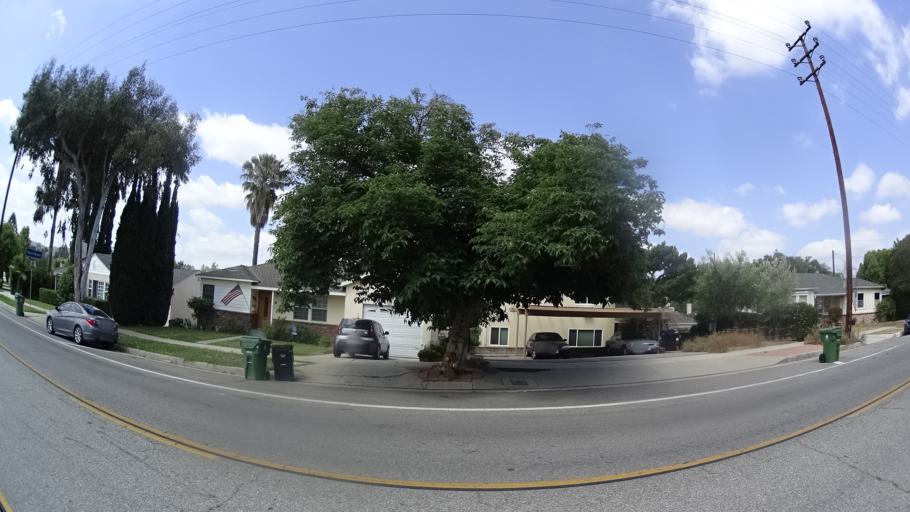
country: US
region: California
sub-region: Los Angeles County
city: Universal City
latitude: 34.1610
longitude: -118.3530
